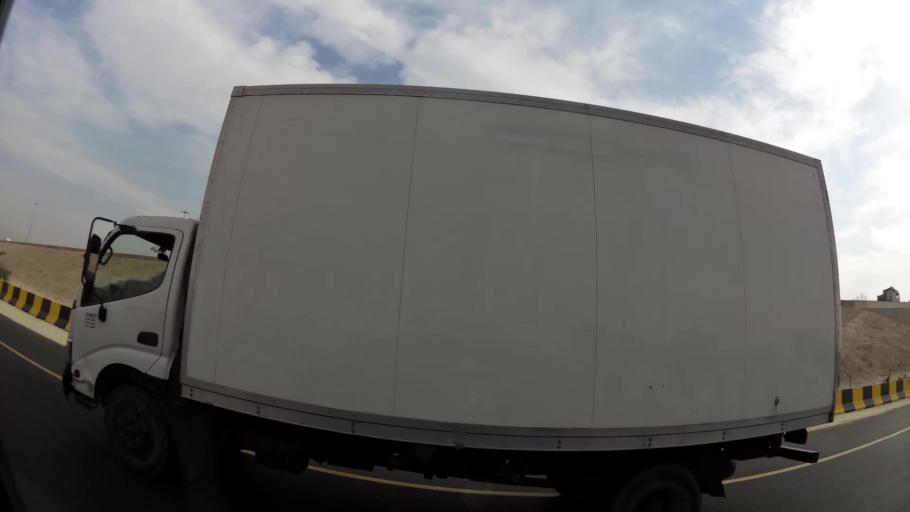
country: KW
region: Muhafazat al Jahra'
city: Al Jahra'
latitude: 29.2824
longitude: 47.7901
